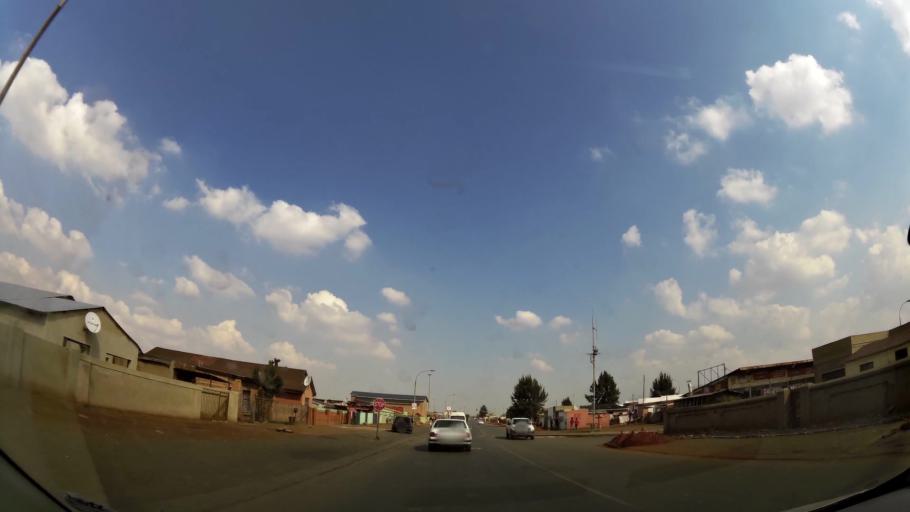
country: ZA
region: Gauteng
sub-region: Ekurhuleni Metropolitan Municipality
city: Germiston
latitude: -26.3433
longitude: 28.1379
